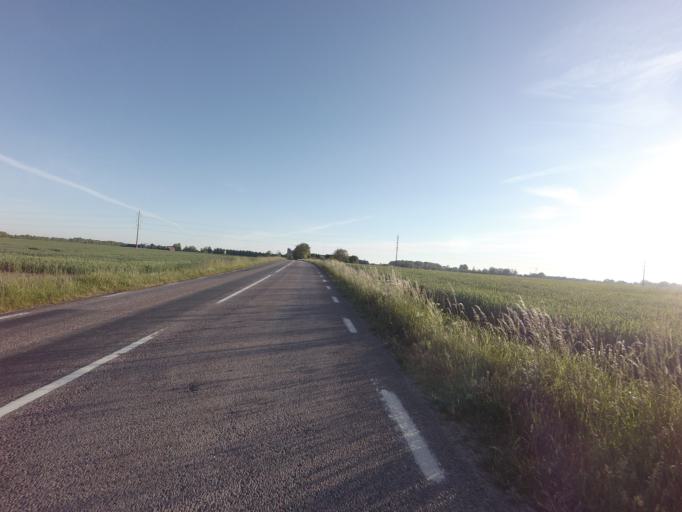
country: SE
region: Skane
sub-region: Helsingborg
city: Odakra
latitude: 56.1703
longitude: 12.6789
